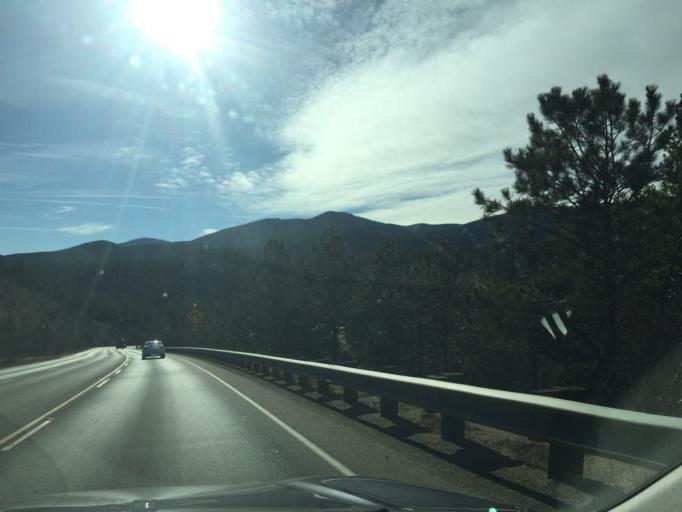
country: US
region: Colorado
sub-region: Jefferson County
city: Evergreen
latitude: 39.4100
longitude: -105.4739
